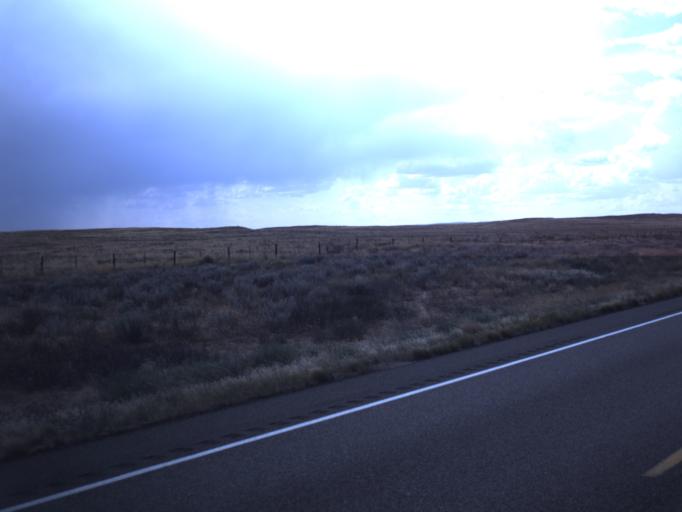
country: US
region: Arizona
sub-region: Coconino County
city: Page
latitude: 37.1034
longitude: -111.8239
